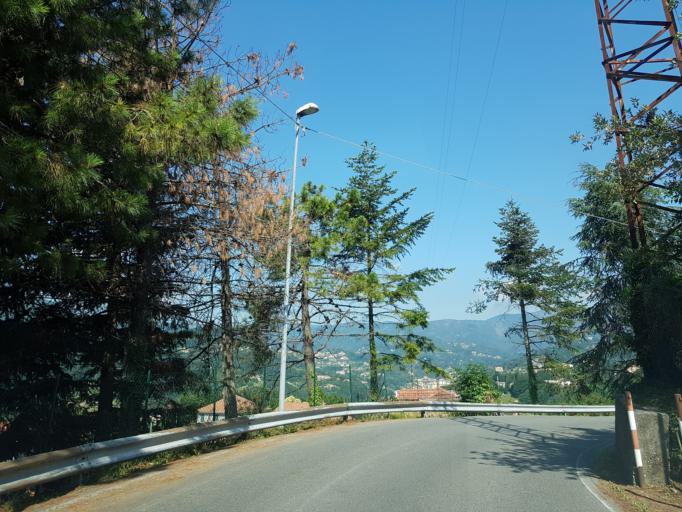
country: IT
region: Liguria
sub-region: Provincia di Genova
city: Pedemonte
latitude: 44.4990
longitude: 8.9100
